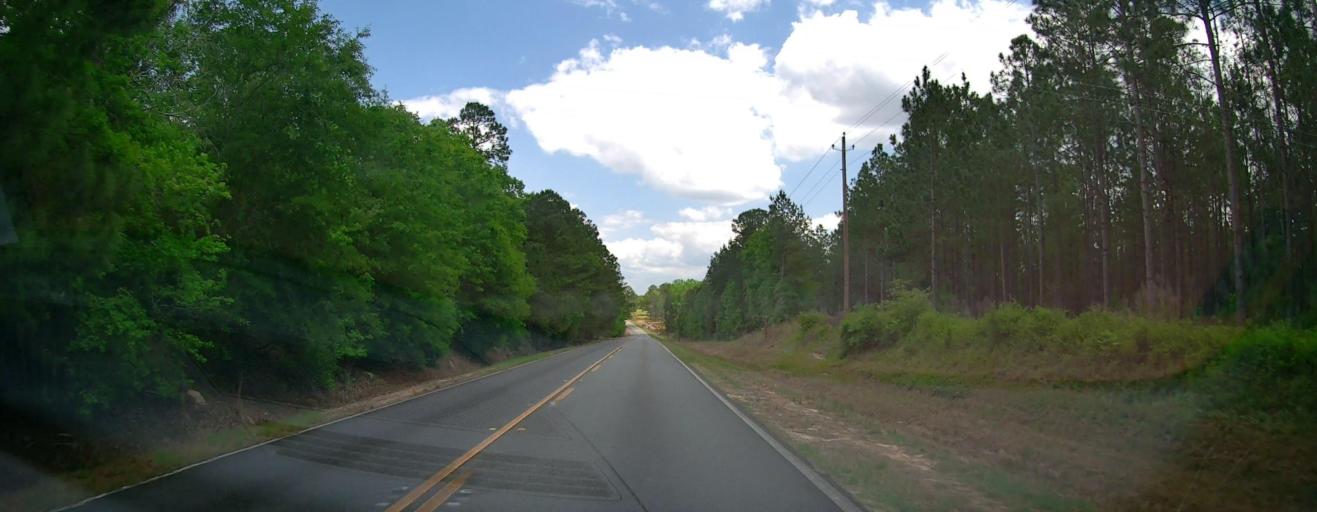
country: US
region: Georgia
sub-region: Laurens County
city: East Dublin
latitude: 32.5256
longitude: -82.7233
